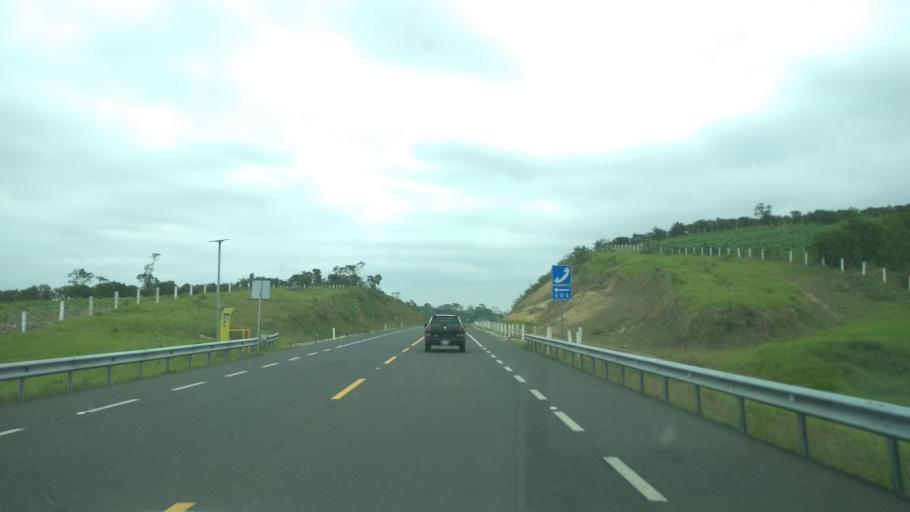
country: MX
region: Veracruz
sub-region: Papantla
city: Polutla
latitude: 20.4429
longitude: -97.2371
